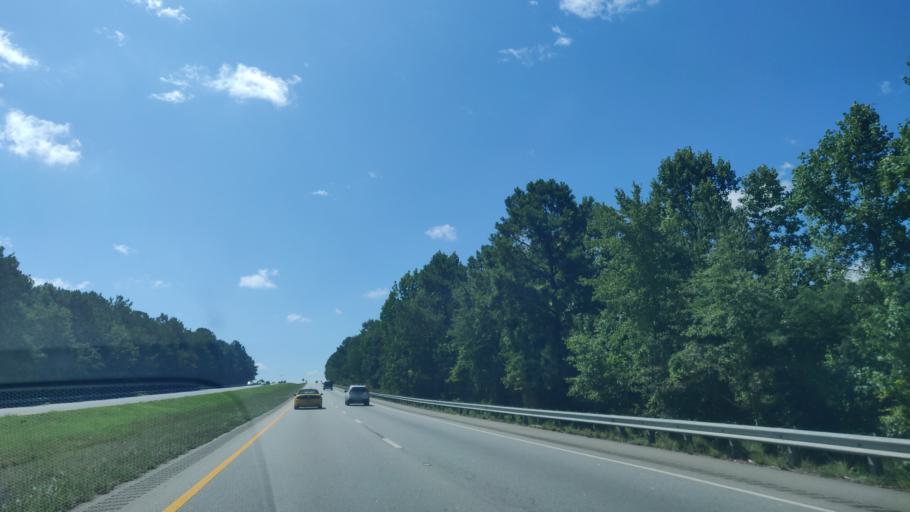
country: US
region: Alabama
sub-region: Lee County
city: Smiths Station
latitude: 32.5168
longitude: -85.0644
